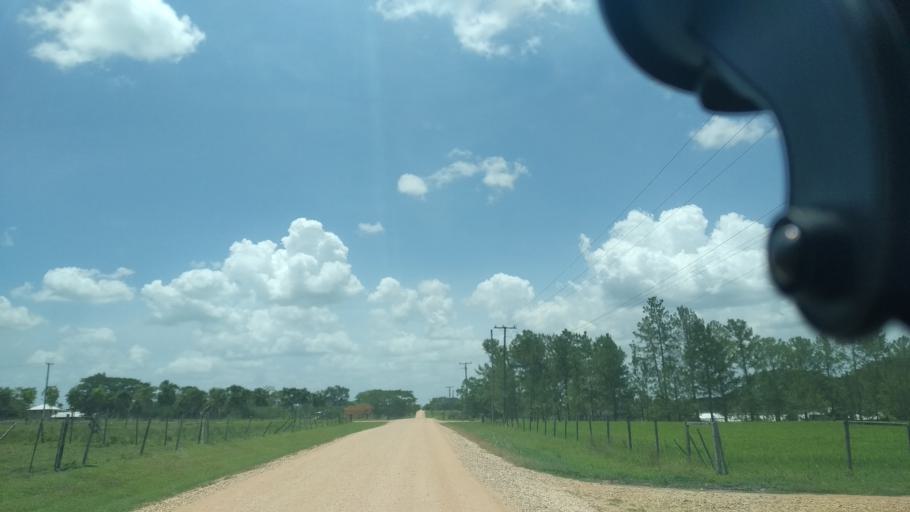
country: BZ
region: Cayo
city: San Ignacio
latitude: 17.2370
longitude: -88.9875
